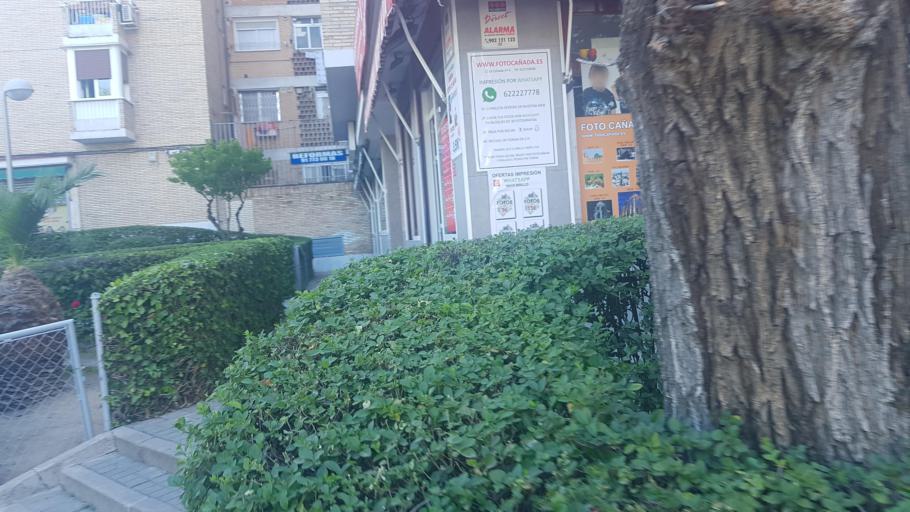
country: ES
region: Madrid
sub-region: Provincia de Madrid
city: Moratalaz
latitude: 40.4038
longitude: -3.6443
